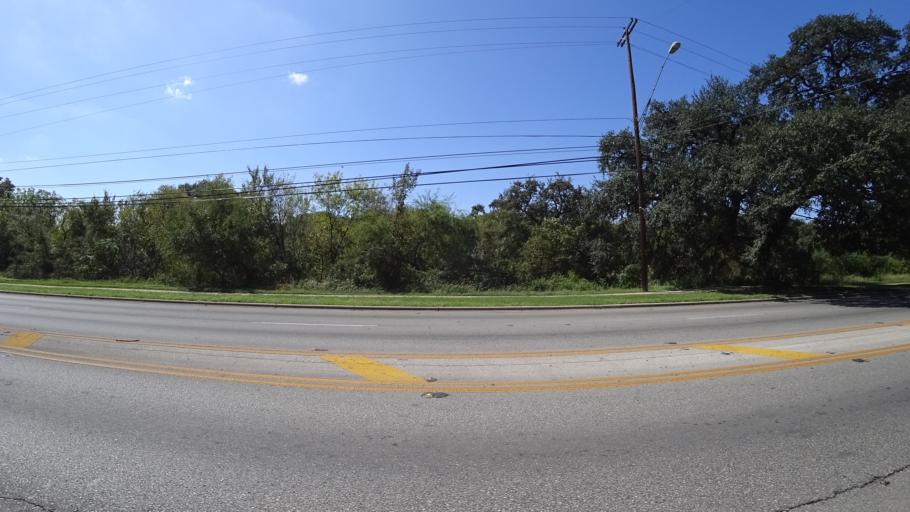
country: US
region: Texas
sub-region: Travis County
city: Austin
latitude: 30.2822
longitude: -97.7508
